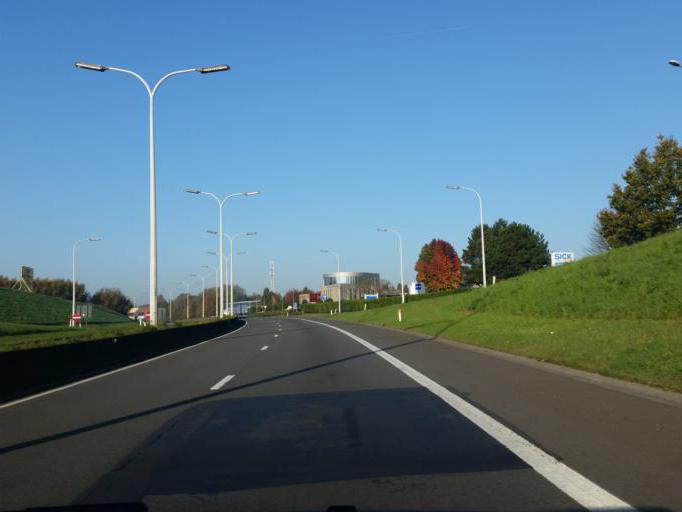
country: BE
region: Flanders
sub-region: Provincie Vlaams-Brabant
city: Wemmel
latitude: 50.8901
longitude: 4.2727
